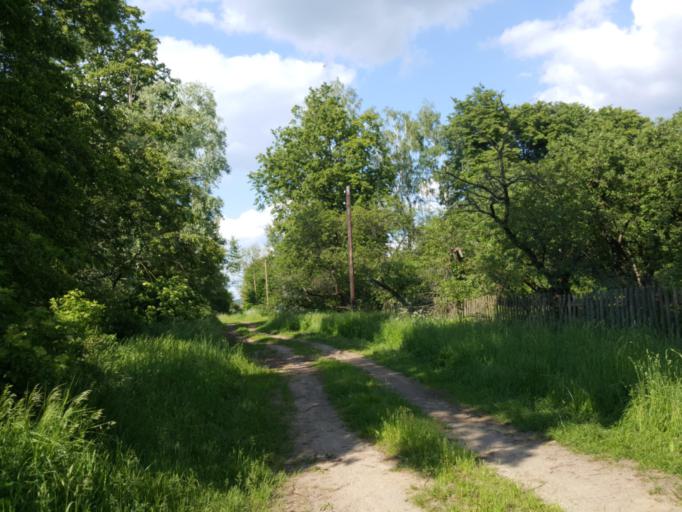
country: BY
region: Brest
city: Kamyanyets
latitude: 52.4509
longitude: 23.6148
